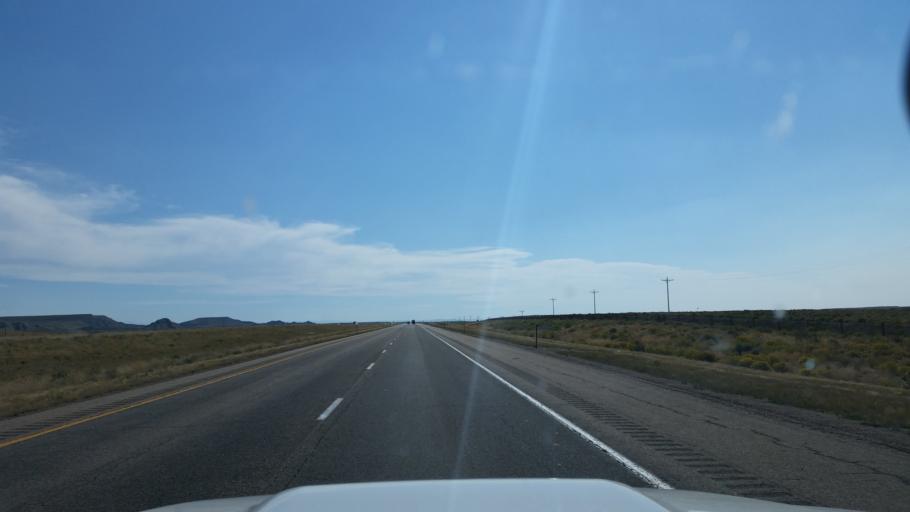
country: US
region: Wyoming
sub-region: Uinta County
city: Lyman
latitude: 41.4499
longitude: -110.0757
